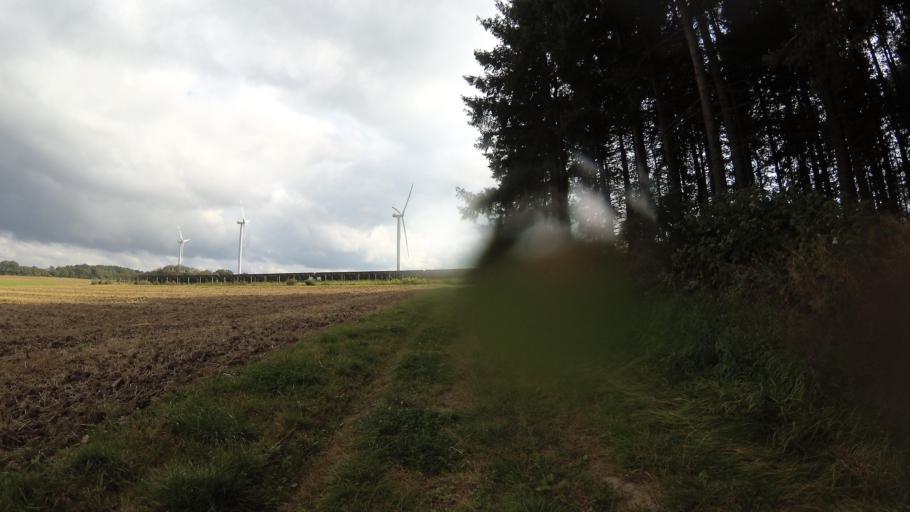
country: DE
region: Saarland
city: Freisen
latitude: 49.5079
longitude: 7.2442
